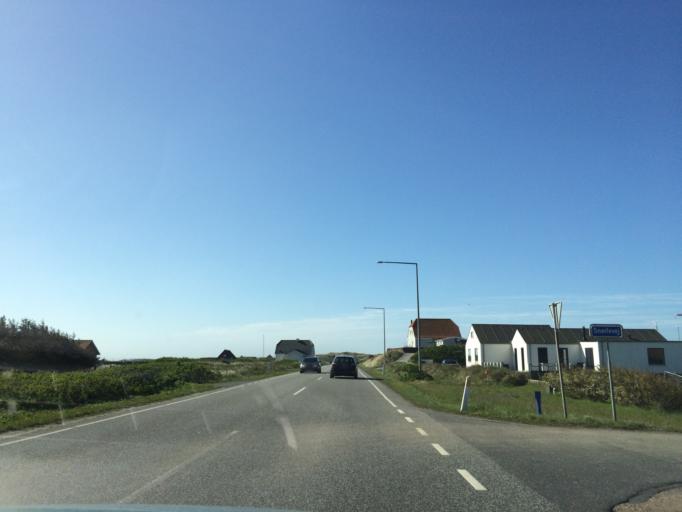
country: DK
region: Central Jutland
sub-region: Ringkobing-Skjern Kommune
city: Hvide Sande
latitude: 55.9803
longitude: 8.1393
